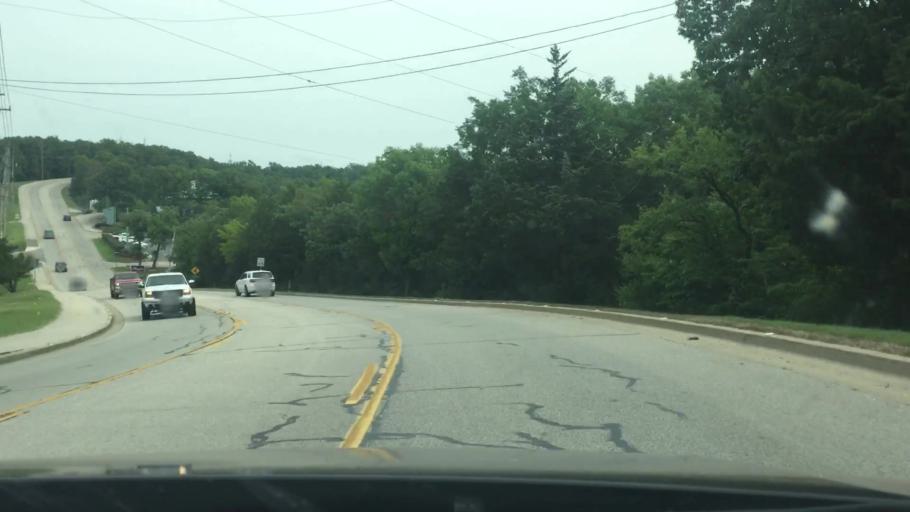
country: US
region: Missouri
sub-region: Camden County
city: Four Seasons
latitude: 38.1908
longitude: -92.6799
